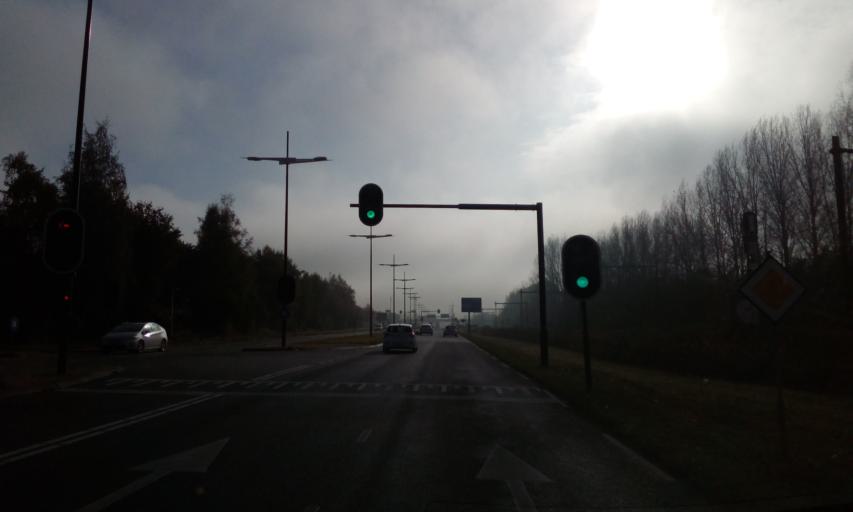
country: NL
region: Gelderland
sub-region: Gemeente Lochem
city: Epse
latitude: 52.2415
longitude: 6.2085
